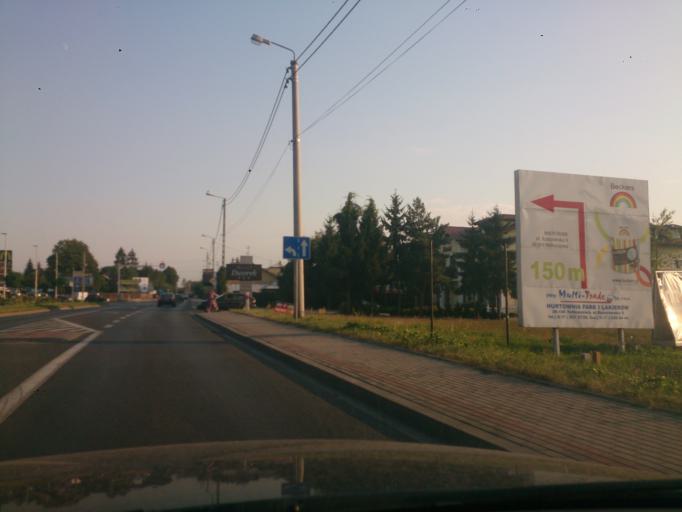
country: PL
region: Subcarpathian Voivodeship
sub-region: Powiat kolbuszowski
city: Kolbuszowa
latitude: 50.2421
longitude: 21.7795
